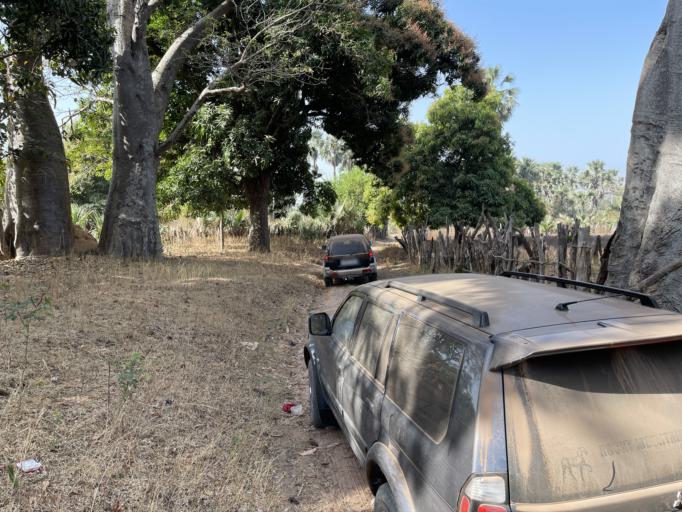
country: GW
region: Oio
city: Farim
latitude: 12.4589
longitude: -15.4069
